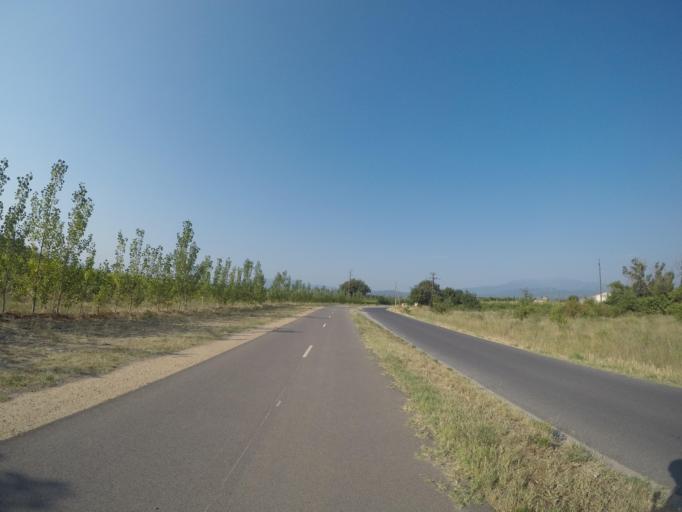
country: FR
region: Languedoc-Roussillon
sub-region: Departement des Pyrenees-Orientales
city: Ponteilla
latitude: 42.6250
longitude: 2.7997
